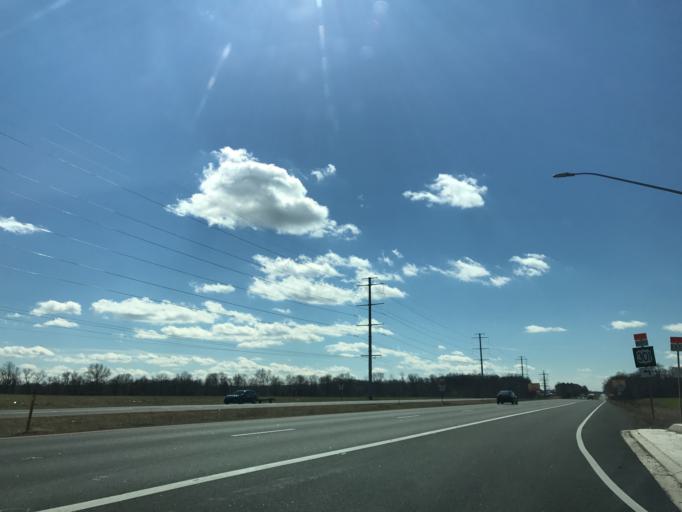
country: US
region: Maryland
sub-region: Queen Anne's County
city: Centreville
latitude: 39.0465
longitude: -76.0088
